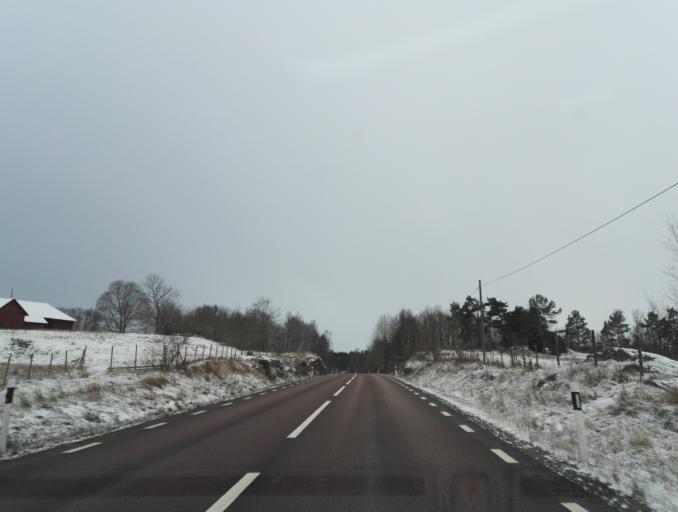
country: SE
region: Kalmar
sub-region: Hultsfreds Kommun
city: Virserum
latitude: 57.2236
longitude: 15.5311
